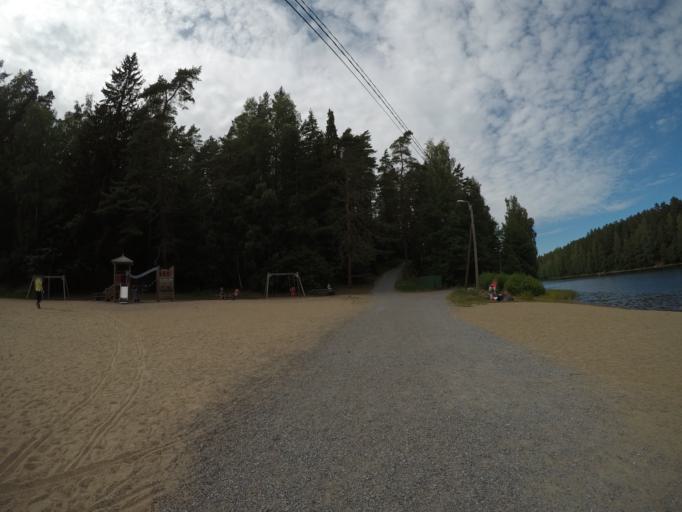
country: FI
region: Haeme
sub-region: Haemeenlinna
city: Haemeenlinna
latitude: 60.9927
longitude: 24.4188
